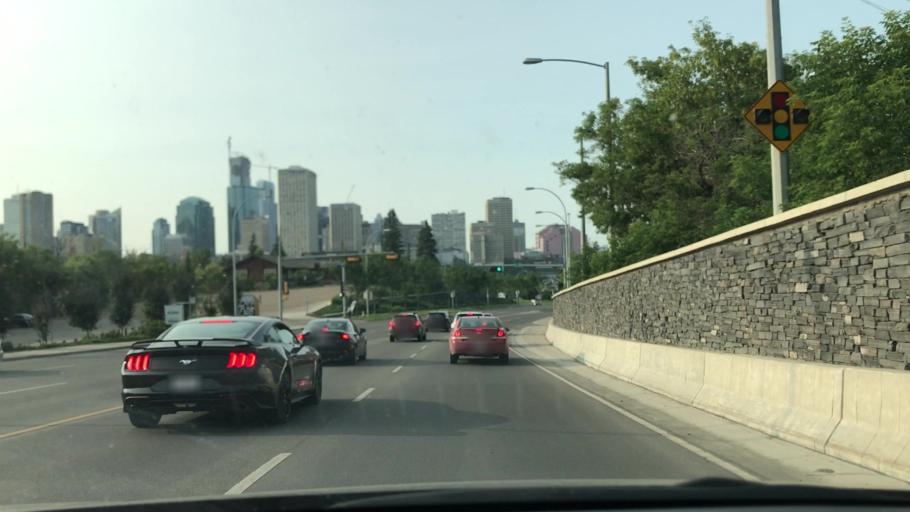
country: CA
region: Alberta
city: Edmonton
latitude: 53.5303
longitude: -113.4853
